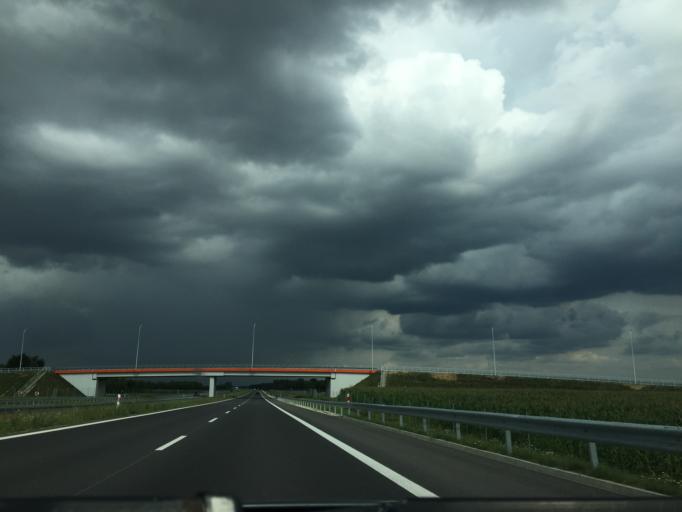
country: PL
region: Masovian Voivodeship
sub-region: Powiat szydlowiecki
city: Jastrzab
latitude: 51.2783
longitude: 20.9588
